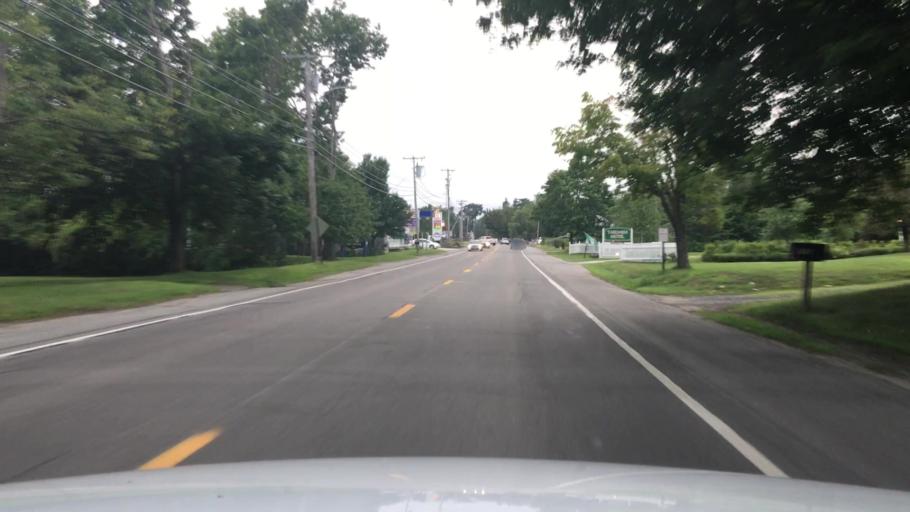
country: US
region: Maine
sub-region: Waldo County
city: Stockton Springs
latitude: 44.4618
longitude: -68.9081
